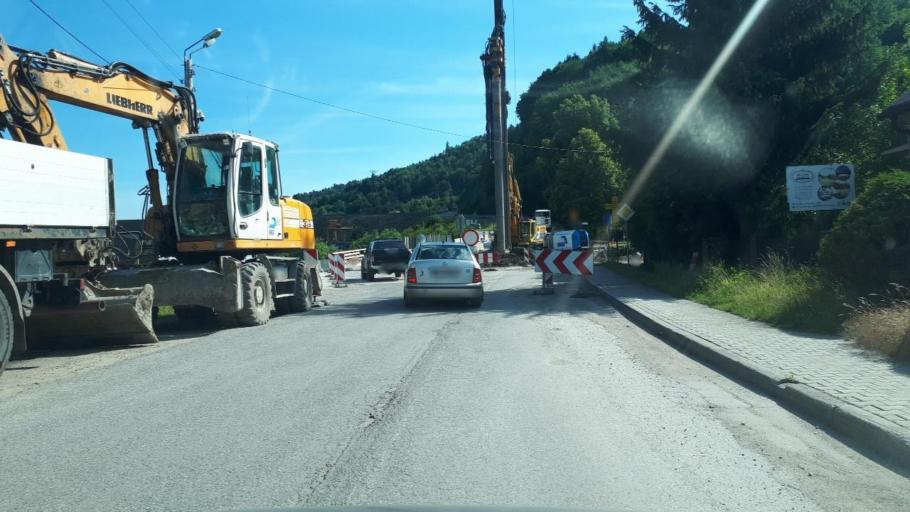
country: PL
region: Silesian Voivodeship
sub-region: Powiat zywiecki
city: Czernichow
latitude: 49.7510
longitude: 19.2072
